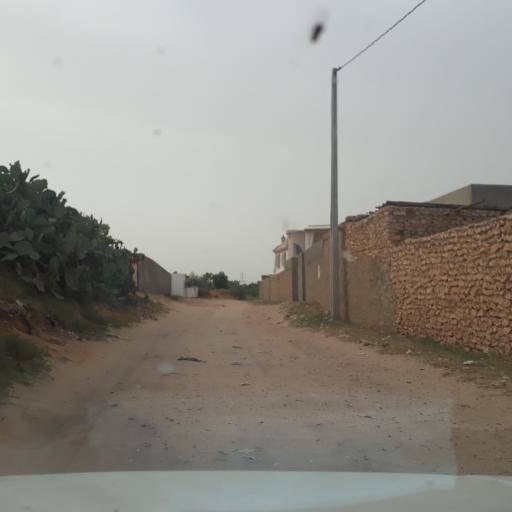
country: TN
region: Safaqis
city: Al Qarmadah
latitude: 34.8254
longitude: 10.7754
